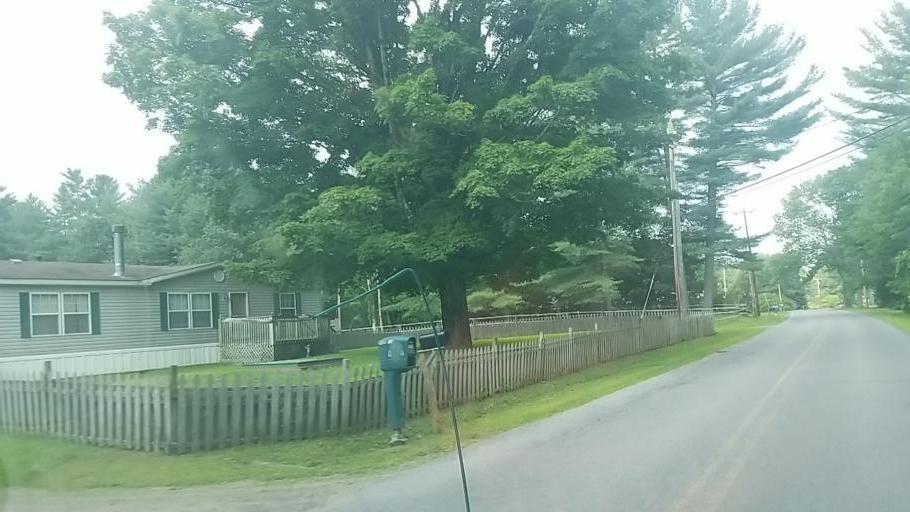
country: US
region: New York
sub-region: Fulton County
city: Broadalbin
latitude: 43.0700
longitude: -74.2470
